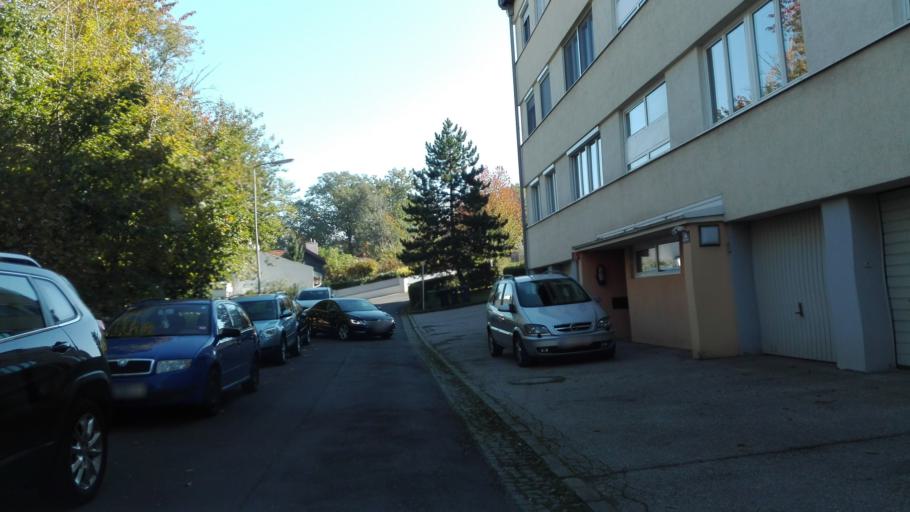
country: AT
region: Upper Austria
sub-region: Politischer Bezirk Linz-Land
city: Leonding
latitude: 48.2838
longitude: 14.2720
